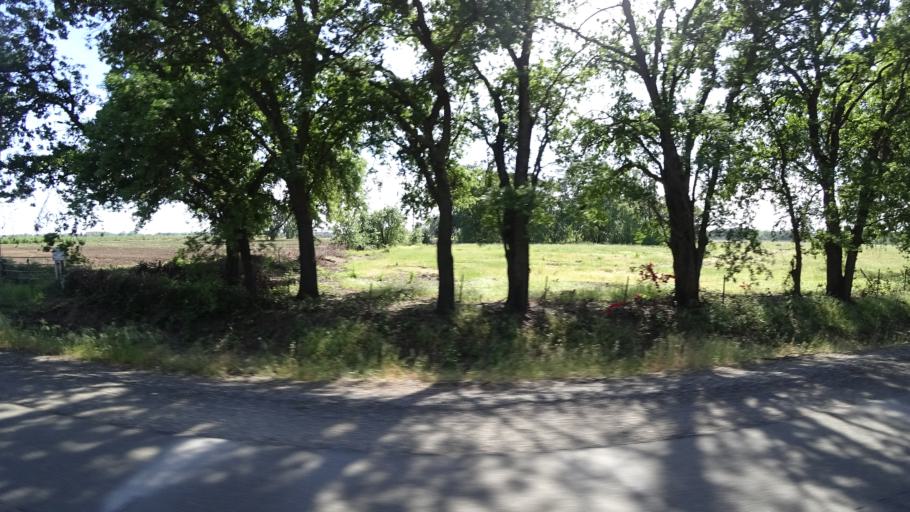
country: US
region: California
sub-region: Tehama County
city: Los Molinos
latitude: 39.9590
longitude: -122.0613
